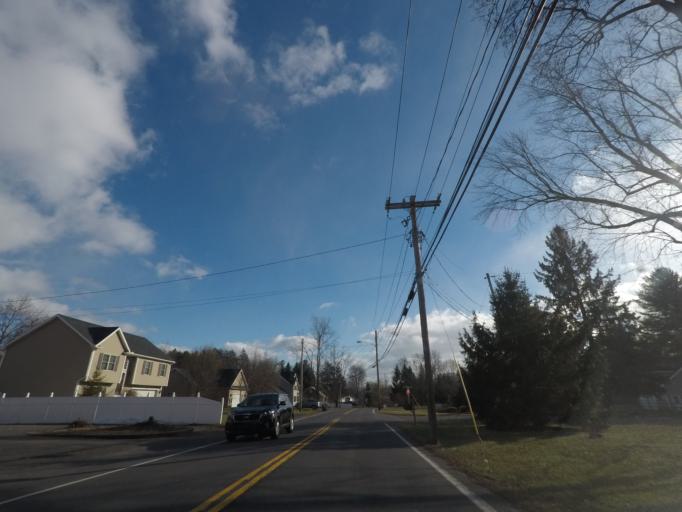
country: US
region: New York
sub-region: Schenectady County
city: Niskayuna
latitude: 42.7534
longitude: -73.8786
